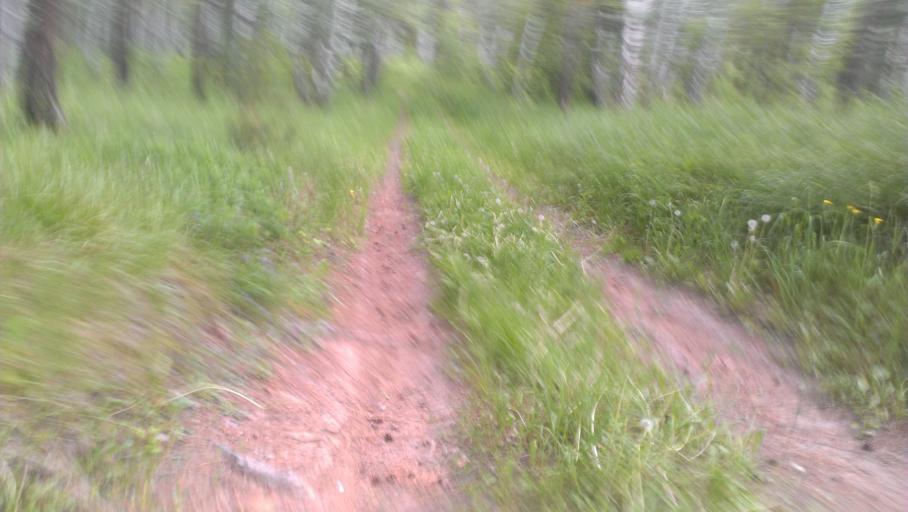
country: RU
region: Altai Krai
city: Sannikovo
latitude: 53.3404
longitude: 84.0481
